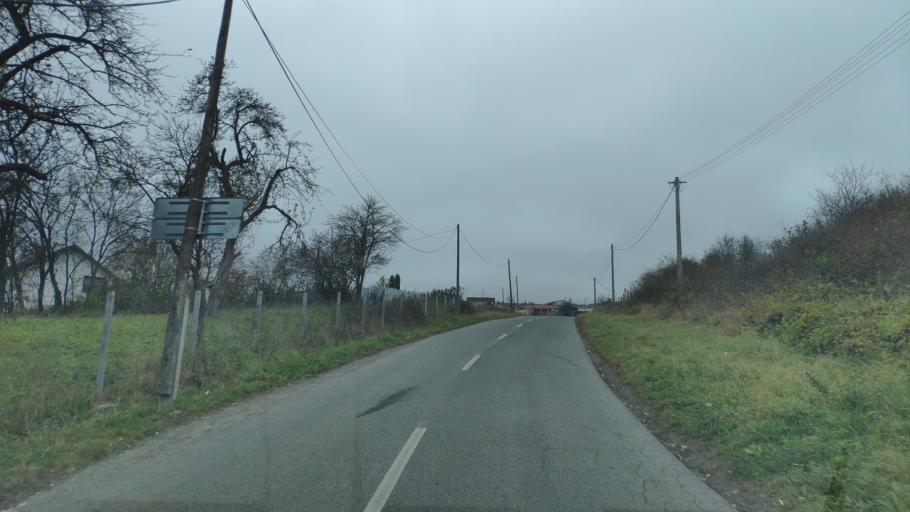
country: SK
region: Presovsky
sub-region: Okres Presov
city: Presov
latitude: 49.1208
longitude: 21.2527
